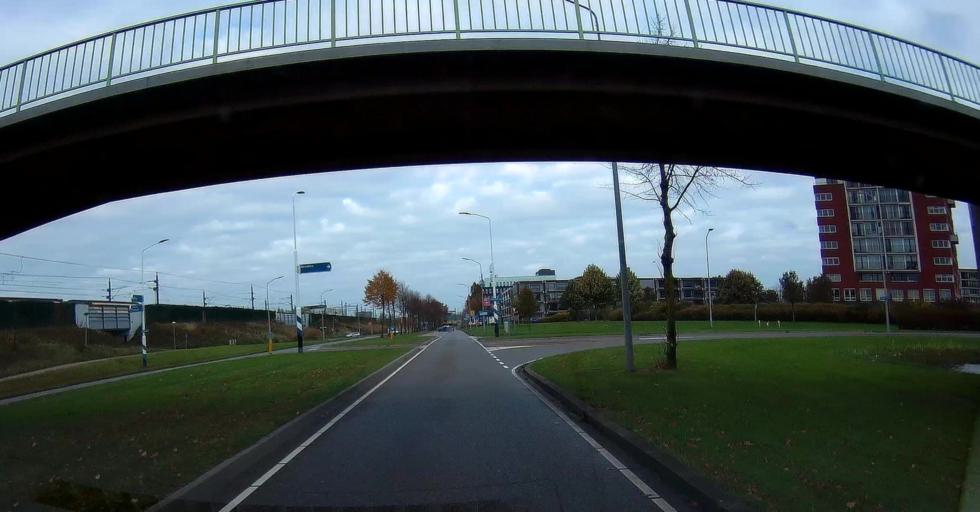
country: NL
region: Flevoland
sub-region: Gemeente Lelystad
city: Lelystad
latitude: 52.5009
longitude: 5.4742
